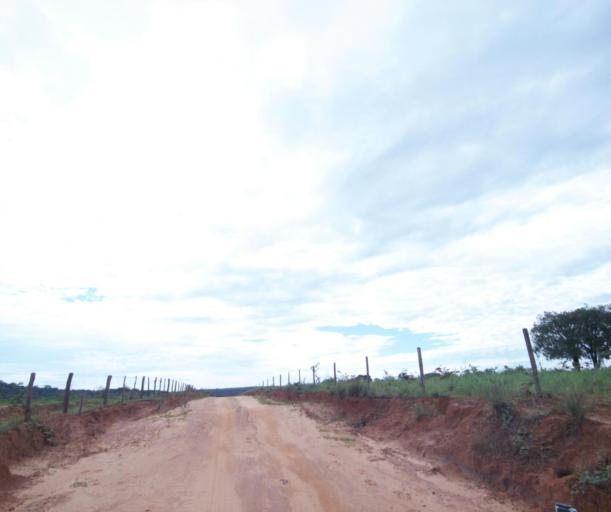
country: BR
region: Bahia
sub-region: Carinhanha
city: Carinhanha
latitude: -14.2081
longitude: -44.4622
